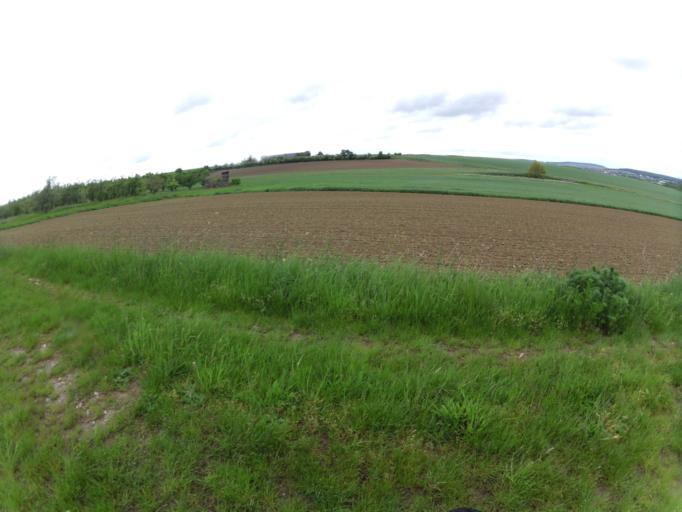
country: DE
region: Bavaria
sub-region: Regierungsbezirk Unterfranken
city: Sommerach
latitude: 49.8421
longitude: 10.2162
